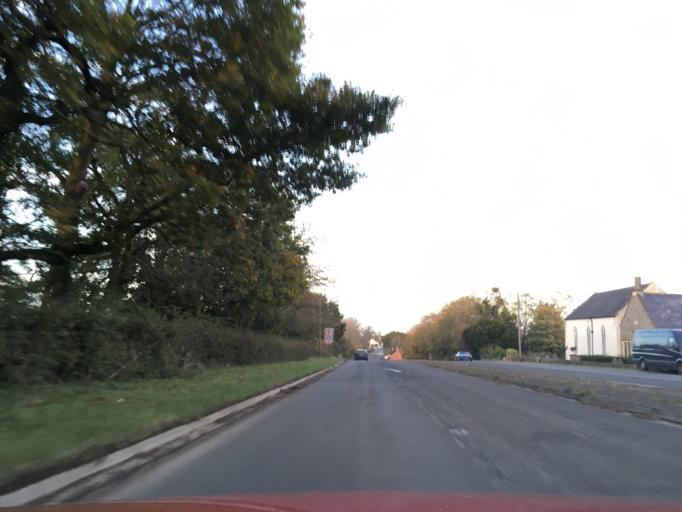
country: GB
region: England
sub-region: South Gloucestershire
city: Falfield
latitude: 51.6306
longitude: -2.4619
